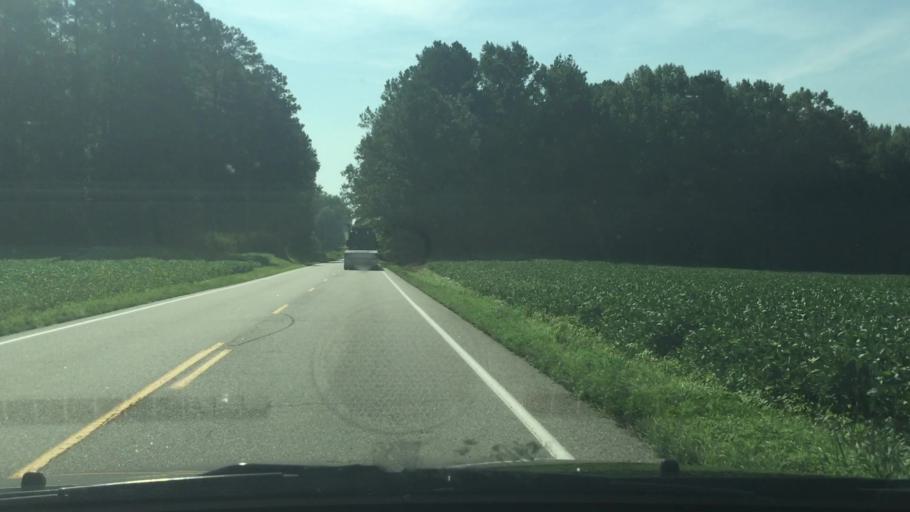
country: US
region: Virginia
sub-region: Prince George County
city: Prince George
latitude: 37.0727
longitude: -77.3451
